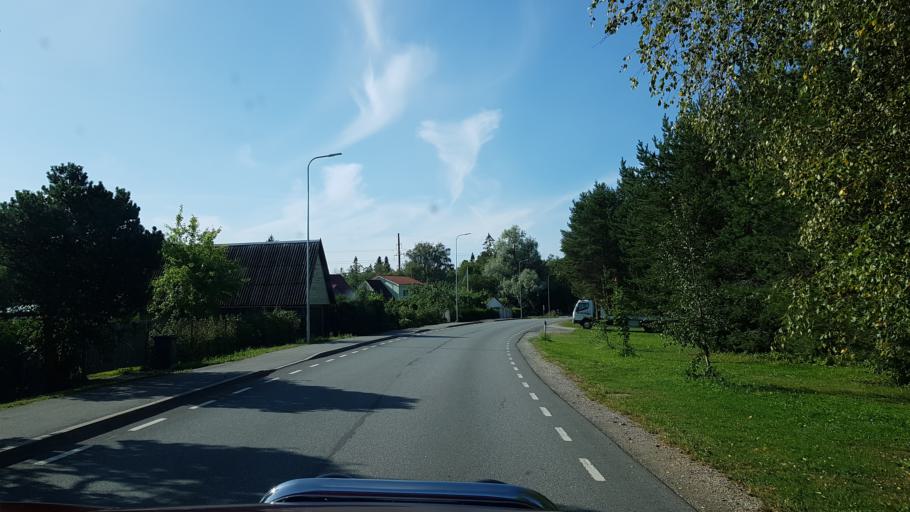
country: EE
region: Harju
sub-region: Joelaehtme vald
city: Loo
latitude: 59.3889
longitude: 24.9353
